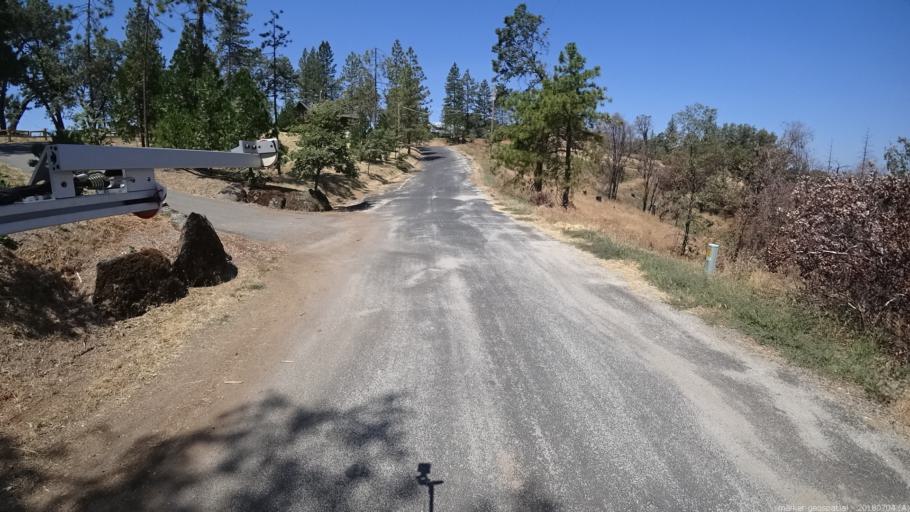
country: US
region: California
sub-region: Fresno County
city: Auberry
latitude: 37.2275
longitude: -119.4671
